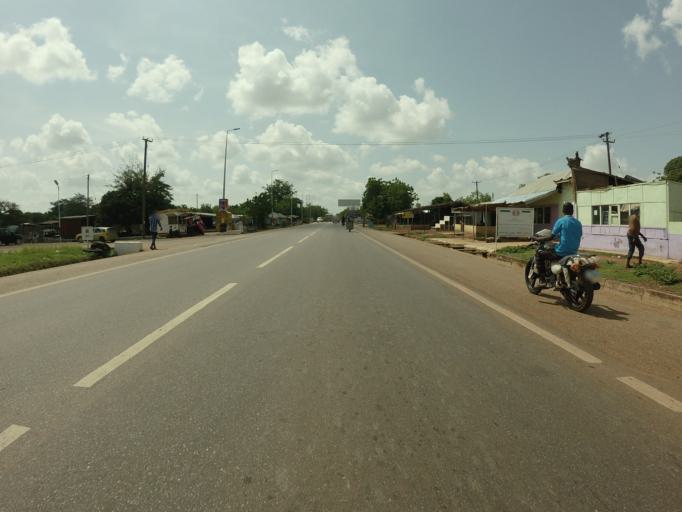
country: GH
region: Northern
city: Tamale
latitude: 9.4519
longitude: -0.8451
